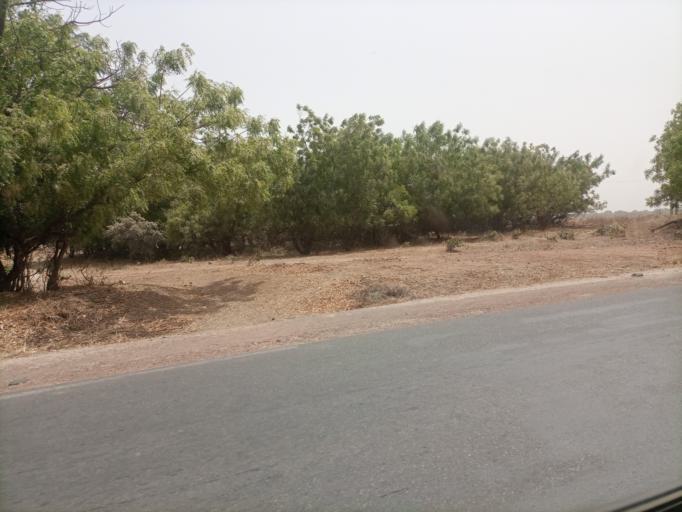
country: SN
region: Fatick
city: Sokone
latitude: 13.7325
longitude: -16.4218
